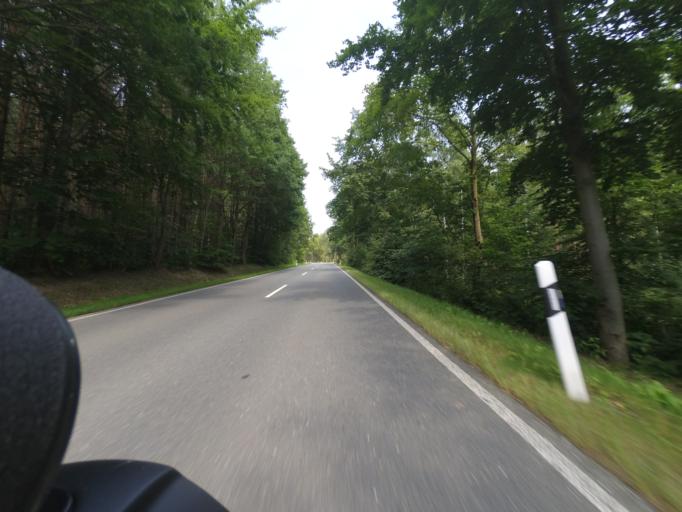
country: DE
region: Thuringia
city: Weissenborn
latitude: 50.9110
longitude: 11.8953
